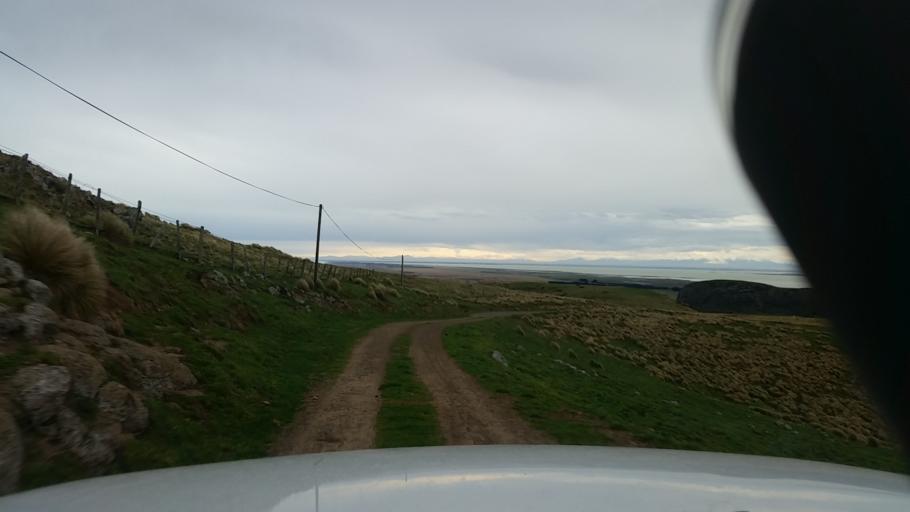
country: NZ
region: Canterbury
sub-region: Selwyn District
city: Lincoln
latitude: -43.8209
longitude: 172.7266
